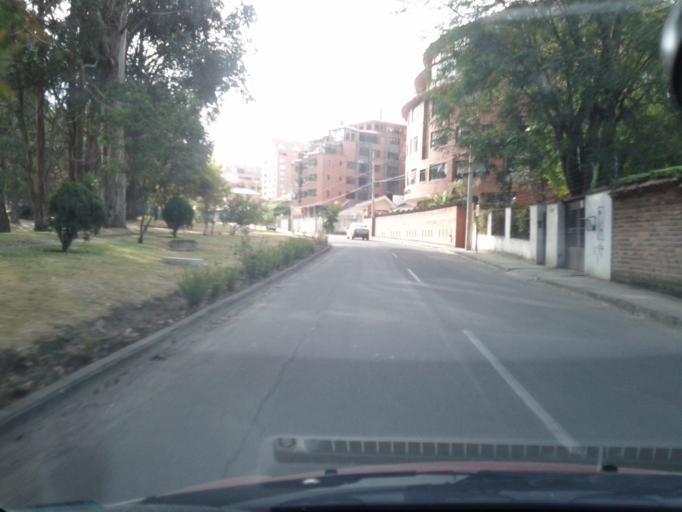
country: EC
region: Azuay
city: Cuenca
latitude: -2.8922
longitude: -79.0274
